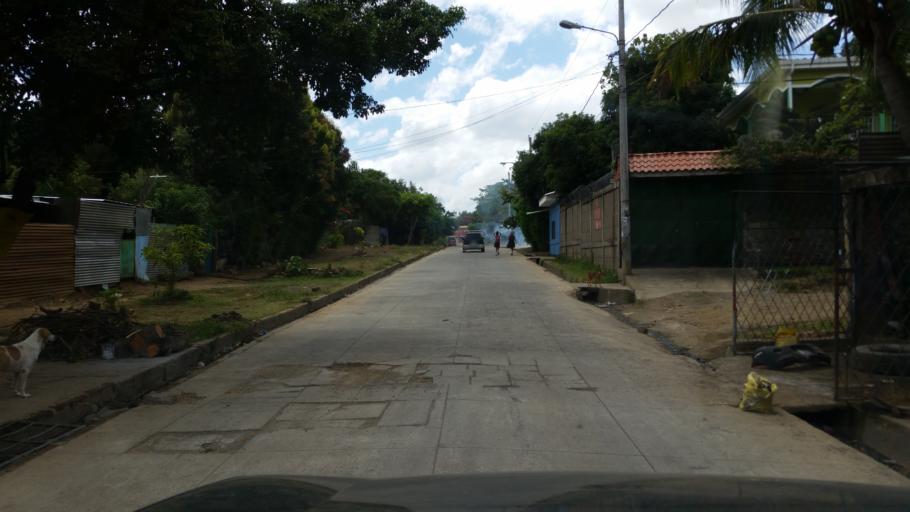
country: NI
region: Managua
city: Managua
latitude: 12.1013
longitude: -86.2251
